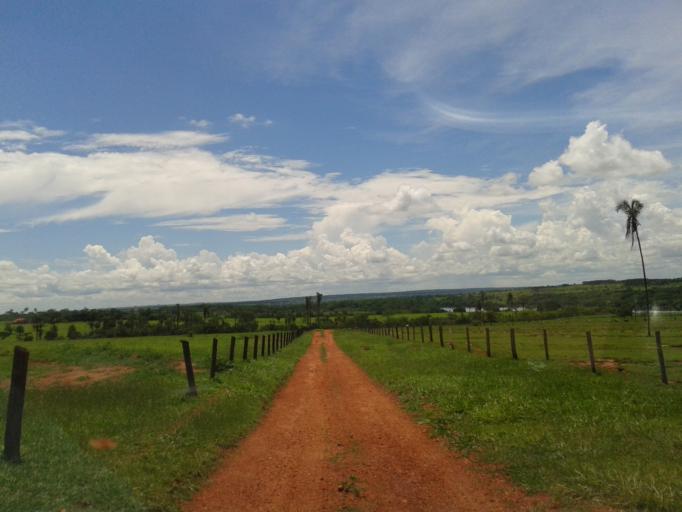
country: BR
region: Minas Gerais
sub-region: Santa Vitoria
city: Santa Vitoria
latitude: -19.1833
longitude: -50.6736
